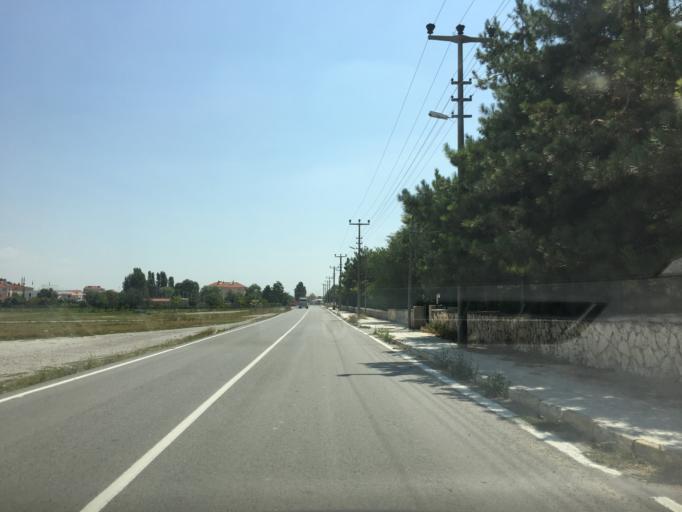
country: TR
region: Eskisehir
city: Cifteler
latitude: 39.3701
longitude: 31.0315
